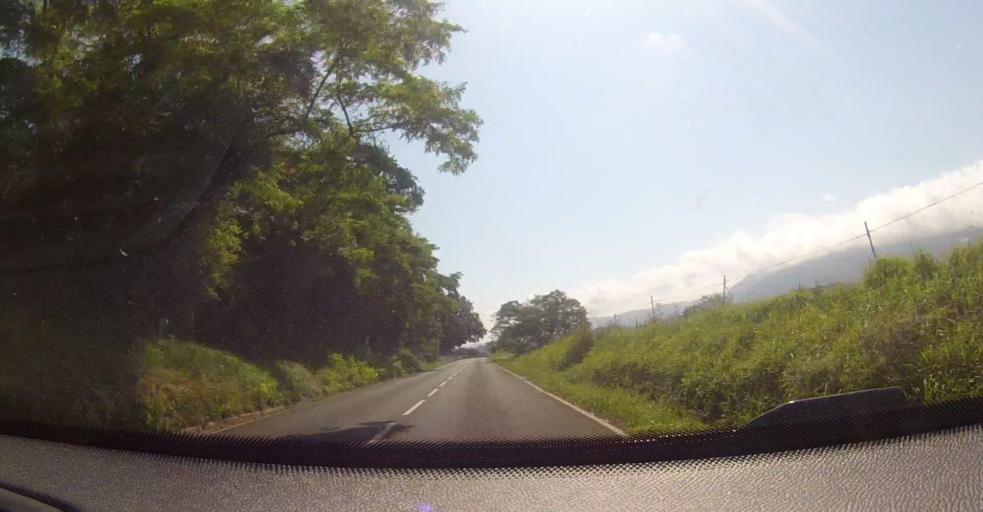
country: ES
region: Asturias
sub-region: Province of Asturias
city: Colunga
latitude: 43.4880
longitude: -5.2983
